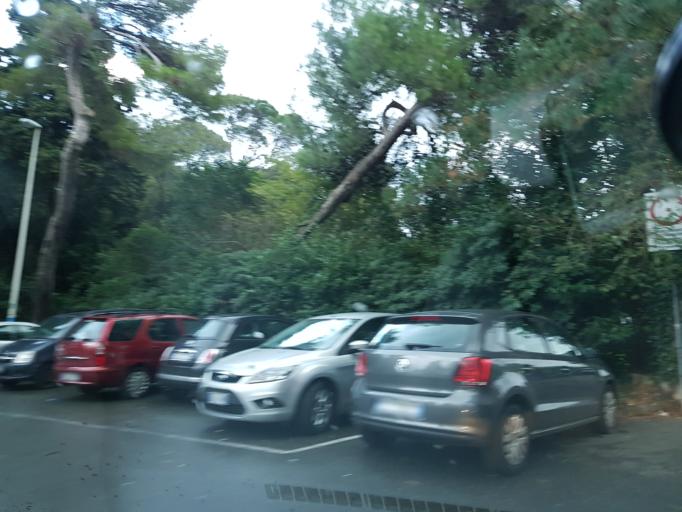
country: IT
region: Liguria
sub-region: Provincia di Genova
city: Genoa
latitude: 44.4005
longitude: 8.9709
